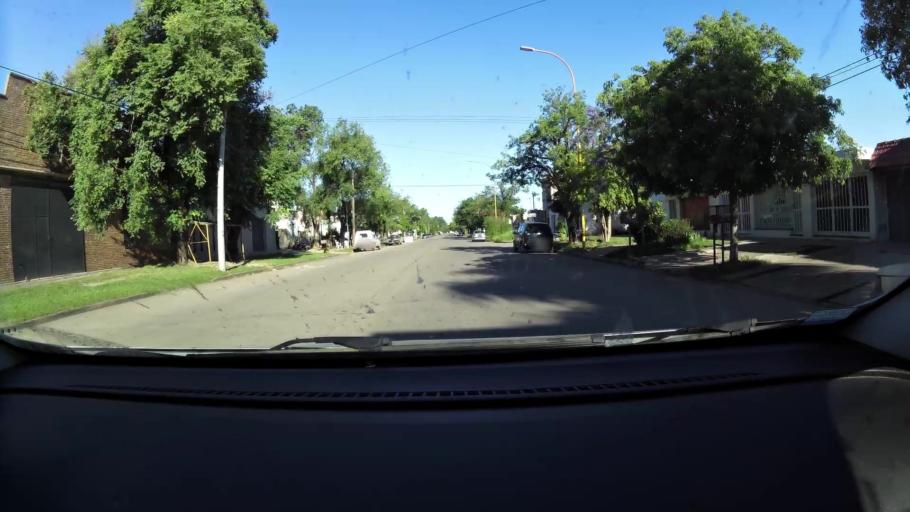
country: AR
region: Cordoba
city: San Francisco
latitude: -31.4328
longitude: -62.0735
